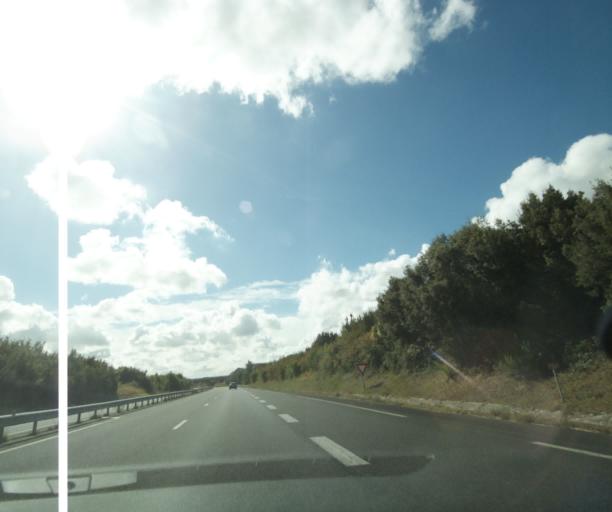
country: FR
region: Poitou-Charentes
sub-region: Departement de la Charente-Maritime
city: Saint-Savinien
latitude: 45.8639
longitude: -0.7319
